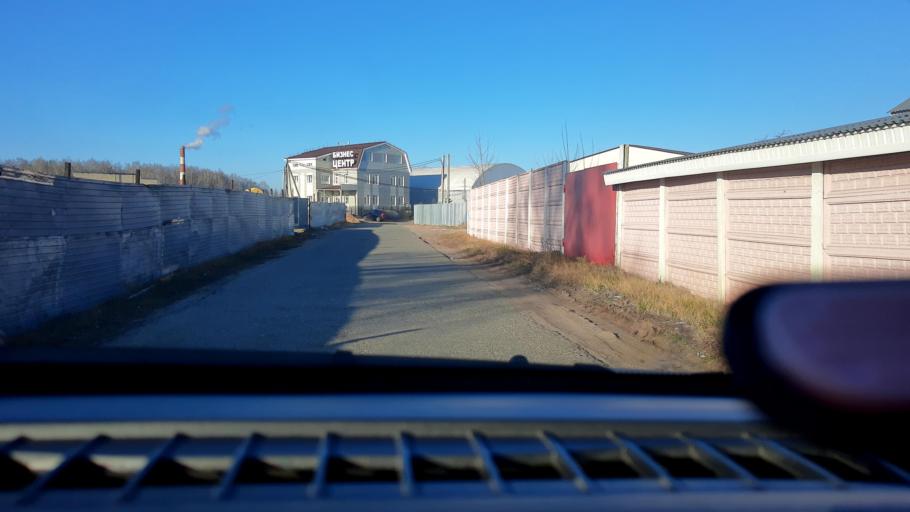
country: RU
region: Nizjnij Novgorod
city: Gorbatovka
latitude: 56.3828
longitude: 43.7997
